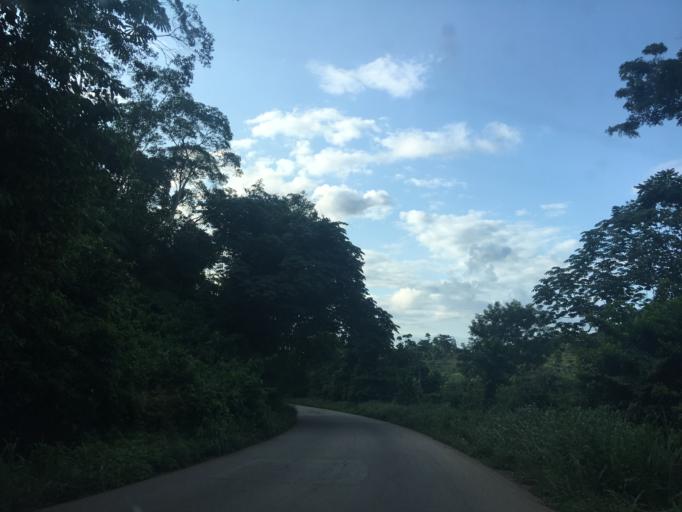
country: GH
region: Western
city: Bibiani
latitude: 6.2792
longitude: -2.2252
